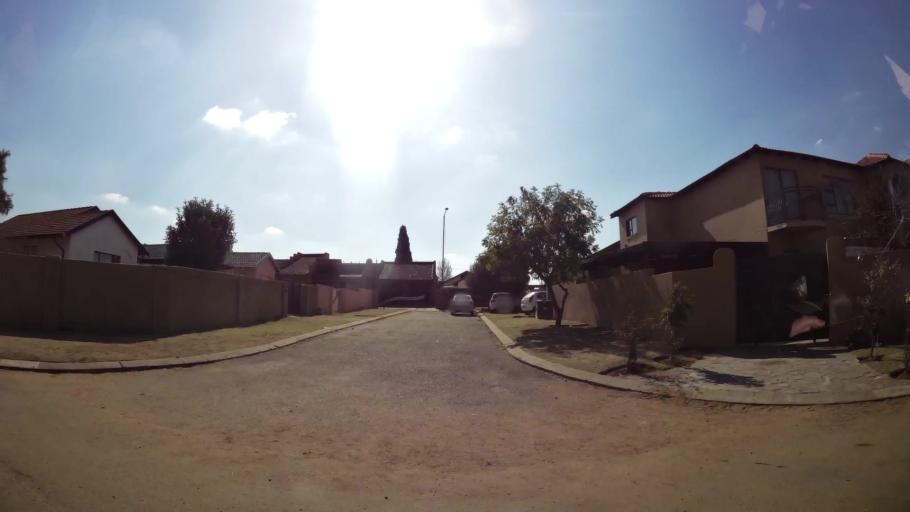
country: ZA
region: Gauteng
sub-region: City of Johannesburg Metropolitan Municipality
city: Roodepoort
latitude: -26.1695
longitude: 27.8010
